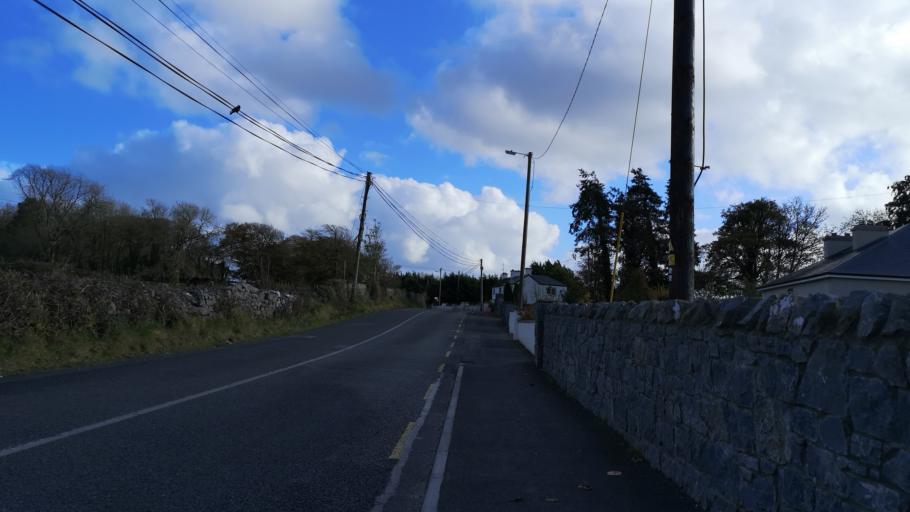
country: IE
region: Connaught
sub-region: County Galway
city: Athenry
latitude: 53.3016
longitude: -8.7654
